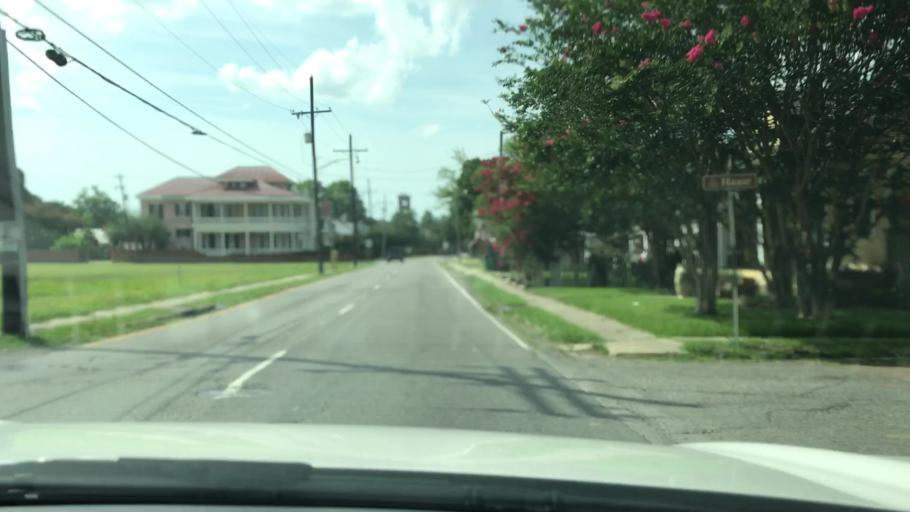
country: US
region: Louisiana
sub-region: Iberville Parish
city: Plaquemine
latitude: 30.2880
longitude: -91.2320
